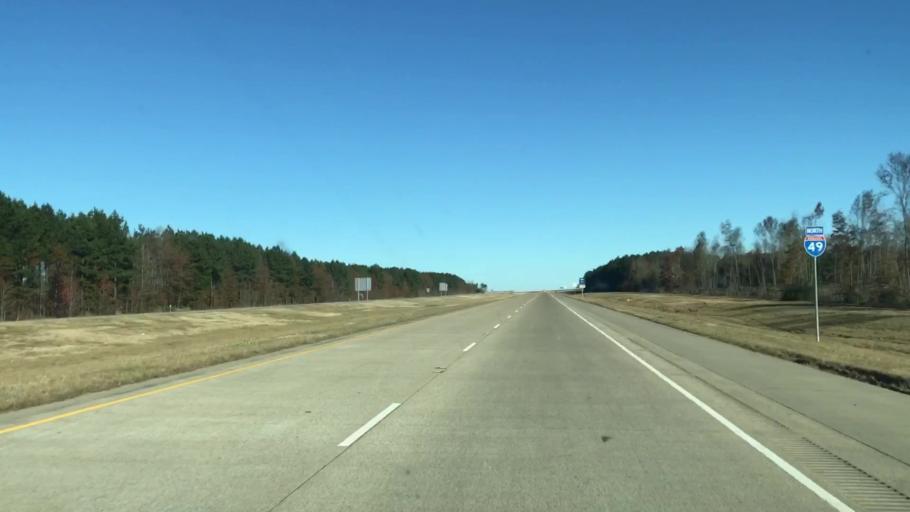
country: US
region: Louisiana
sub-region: Caddo Parish
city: Blanchard
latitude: 32.6044
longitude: -93.8329
